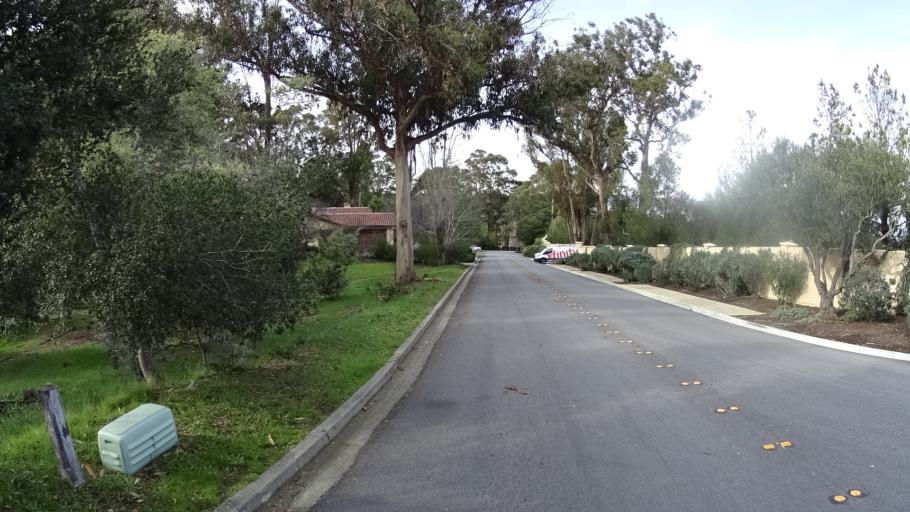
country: US
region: California
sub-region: San Mateo County
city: Hillsborough
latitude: 37.5604
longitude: -122.3689
